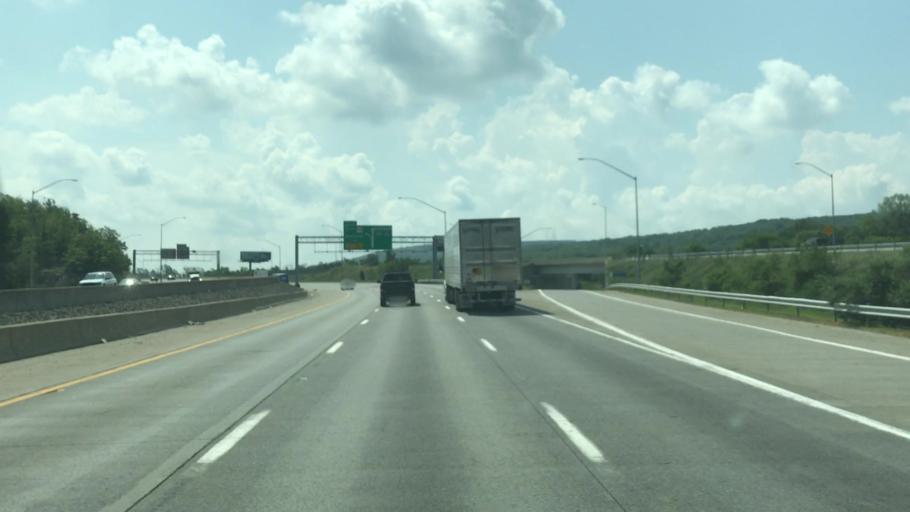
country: US
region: Pennsylvania
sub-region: Lackawanna County
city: Dunmore
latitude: 41.4134
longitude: -75.6006
